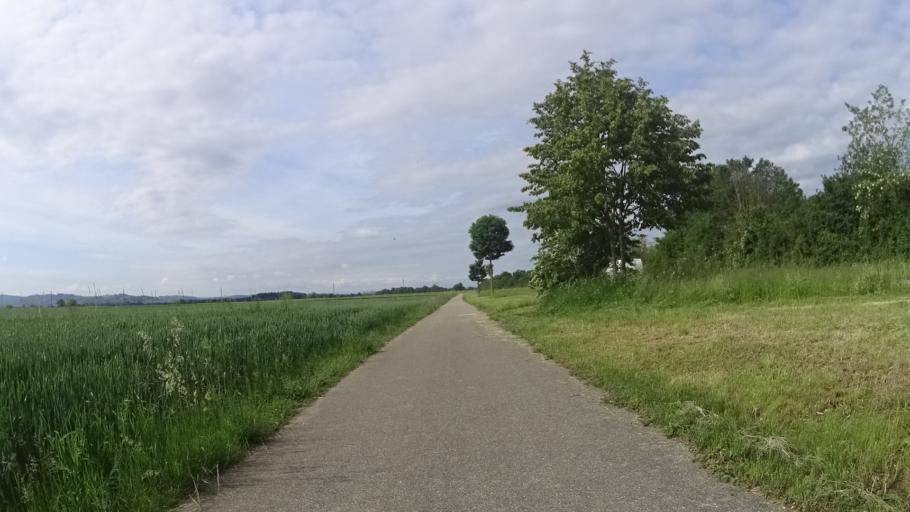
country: DE
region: Baden-Wuerttemberg
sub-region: Freiburg Region
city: Neuenburg am Rhein
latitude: 47.8012
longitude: 7.5608
